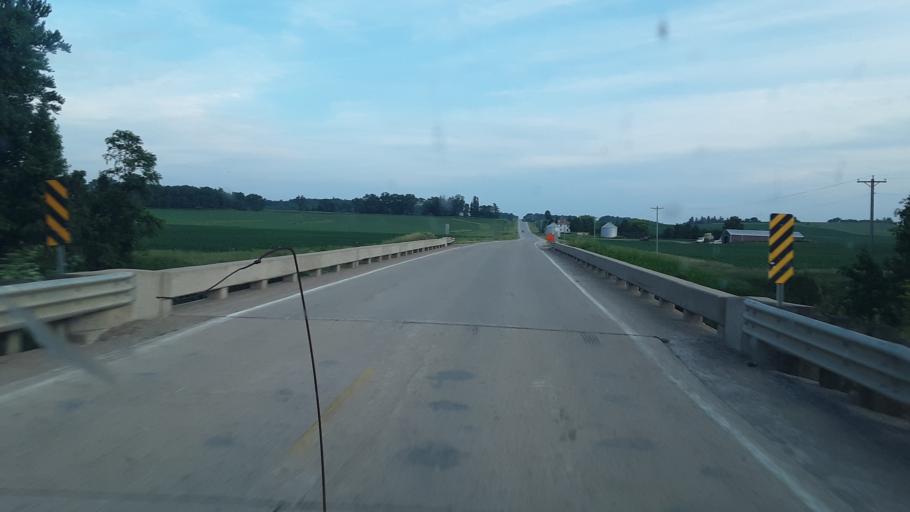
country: US
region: Iowa
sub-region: Iowa County
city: Marengo
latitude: 41.7500
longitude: -92.1821
